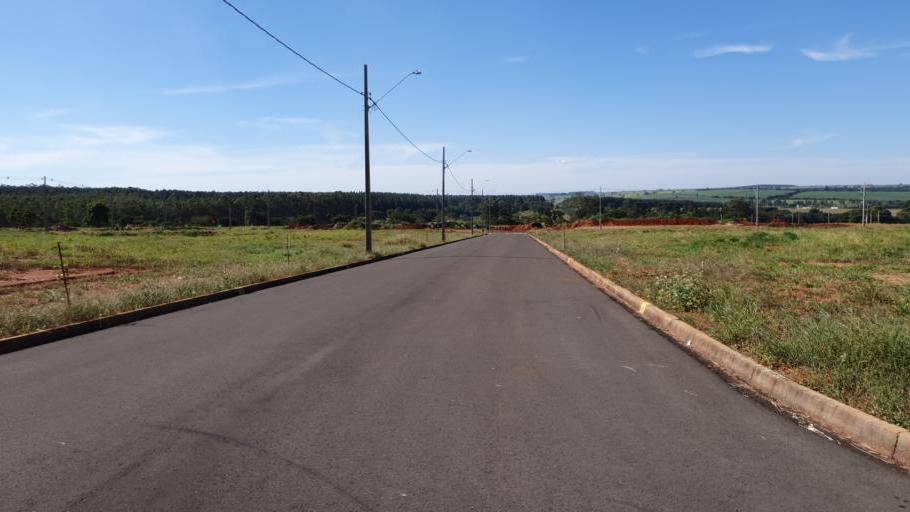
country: BR
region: Sao Paulo
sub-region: Paraguacu Paulista
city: Paraguacu Paulista
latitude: -22.4016
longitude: -50.5757
